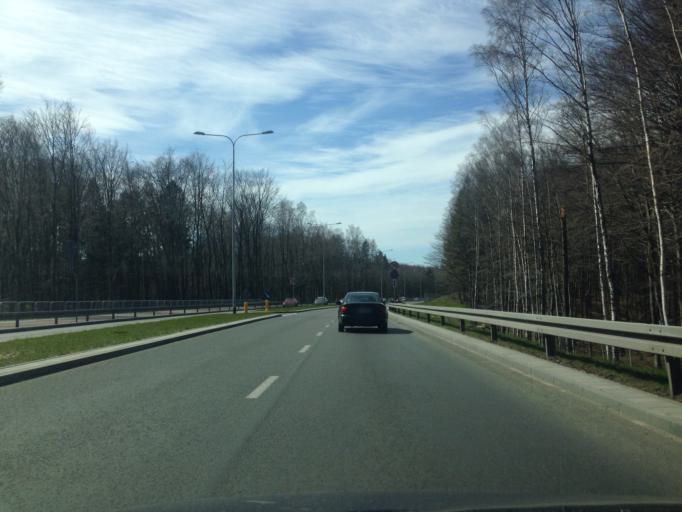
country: PL
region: Pomeranian Voivodeship
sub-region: Gdynia
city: Wielki Kack
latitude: 54.4986
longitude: 18.4900
